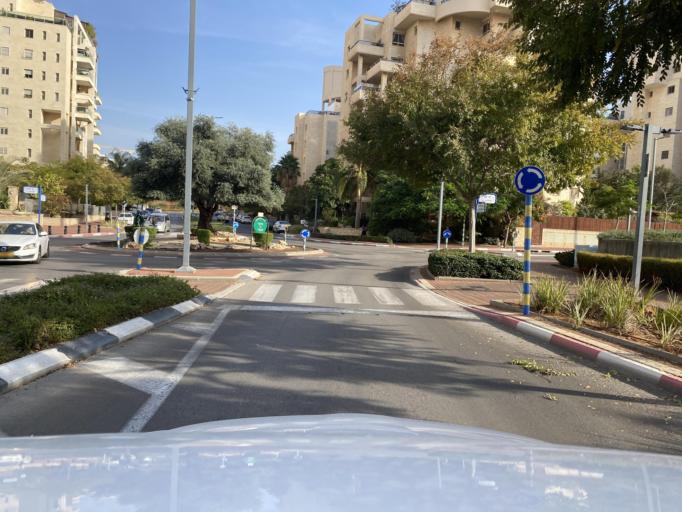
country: IL
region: Tel Aviv
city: Giv`at Shemu'el
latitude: 32.0725
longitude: 34.8545
